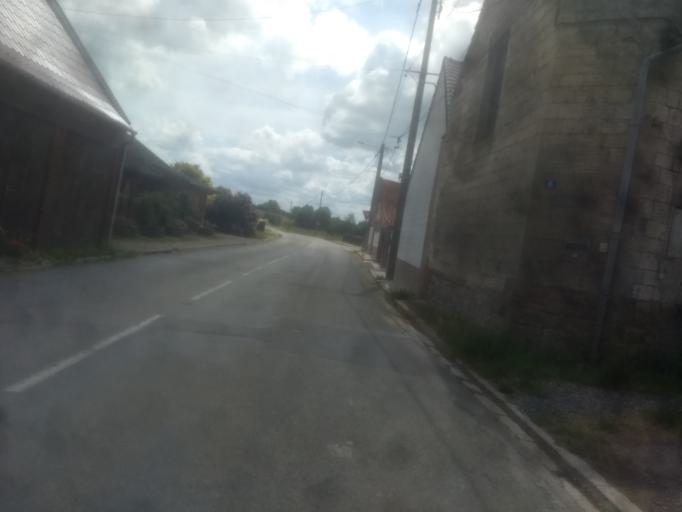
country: FR
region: Nord-Pas-de-Calais
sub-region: Departement du Pas-de-Calais
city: Mont-Saint-Eloi
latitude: 50.3464
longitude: 2.6517
